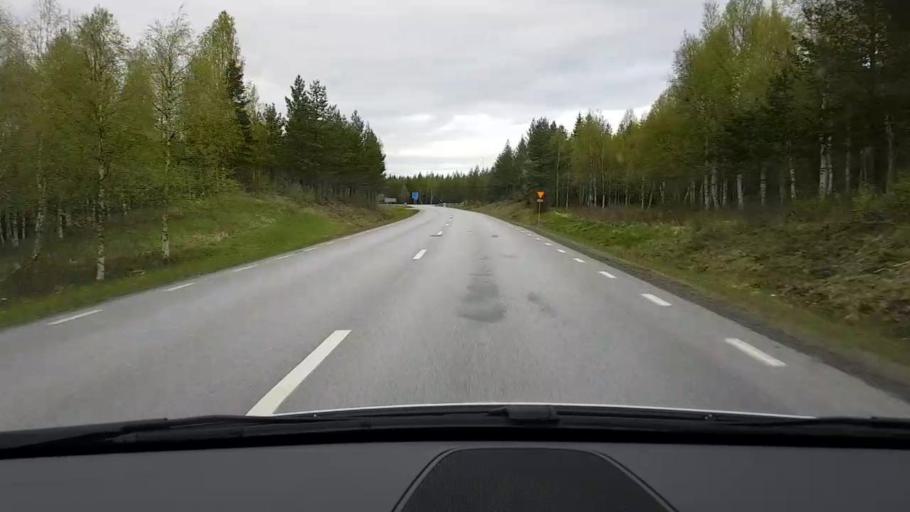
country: SE
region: Jaemtland
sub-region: Krokoms Kommun
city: Valla
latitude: 63.3066
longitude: 13.9221
